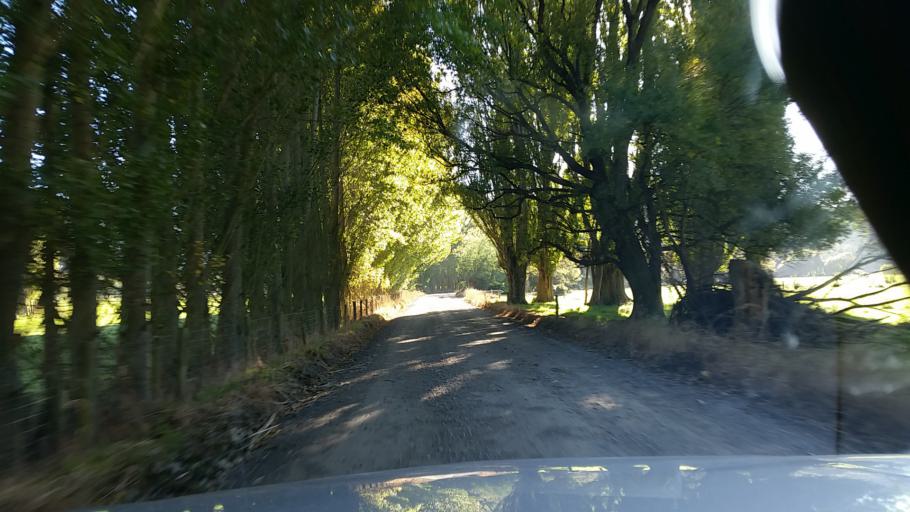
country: NZ
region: Marlborough
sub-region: Marlborough District
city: Blenheim
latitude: -41.4441
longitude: 173.8963
